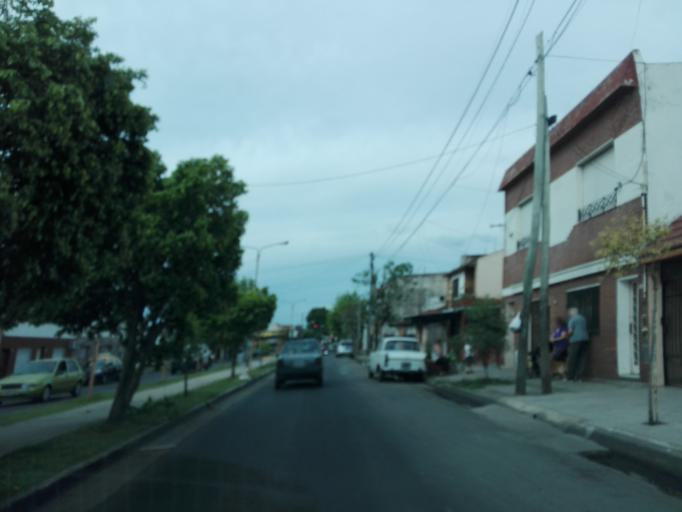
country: AR
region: Buenos Aires
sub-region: Partido de Lanus
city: Lanus
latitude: -34.7121
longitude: -58.3779
